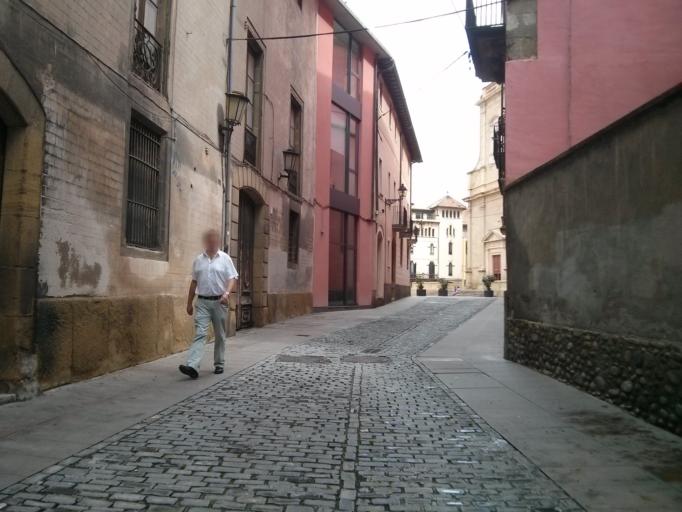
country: ES
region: Catalonia
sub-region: Provincia de Barcelona
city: Vic
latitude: 41.9270
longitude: 2.2545
